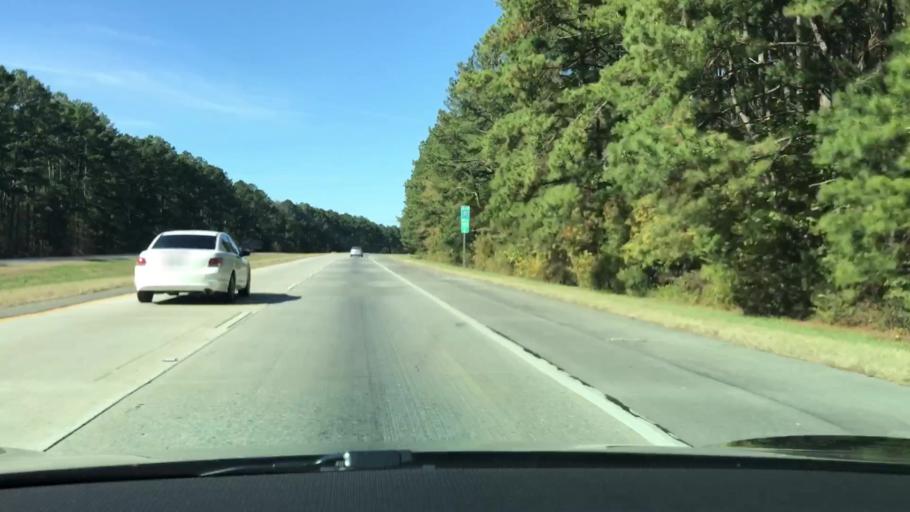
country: US
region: Georgia
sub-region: Taliaferro County
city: Crawfordville
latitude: 33.5315
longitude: -82.9822
